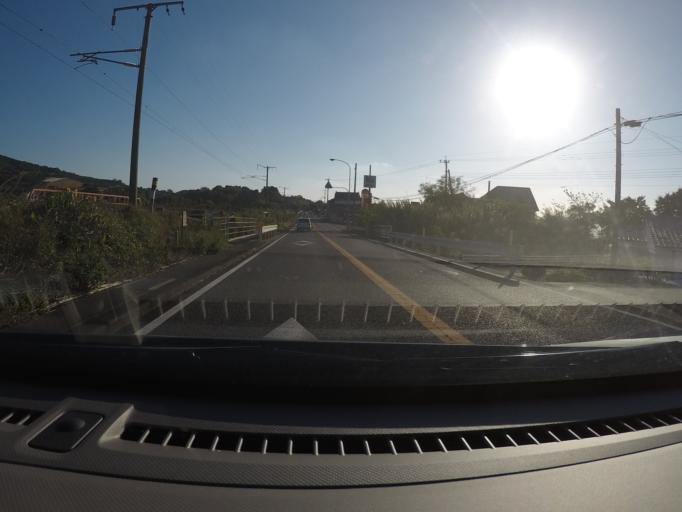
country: JP
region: Kagoshima
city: Izumi
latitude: 32.1403
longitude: 130.3546
